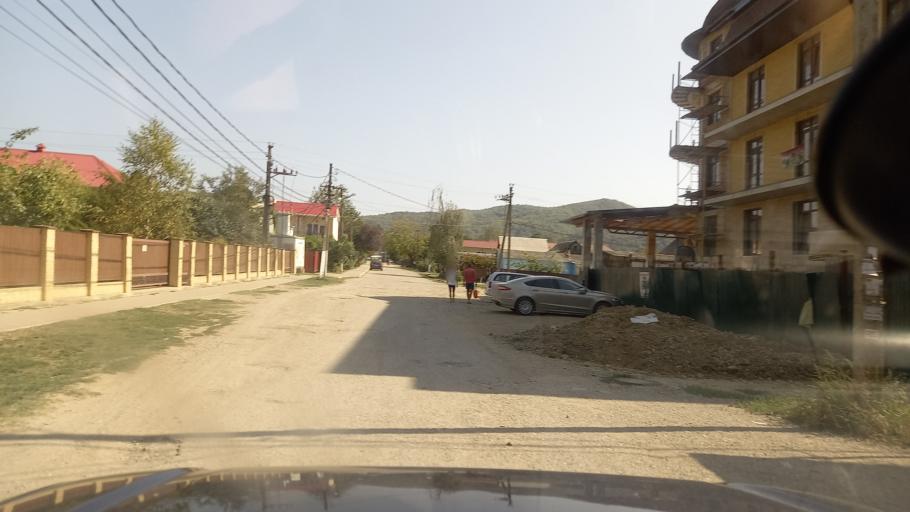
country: RU
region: Krasnodarskiy
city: Arkhipo-Osipovka
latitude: 44.3651
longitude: 38.5248
